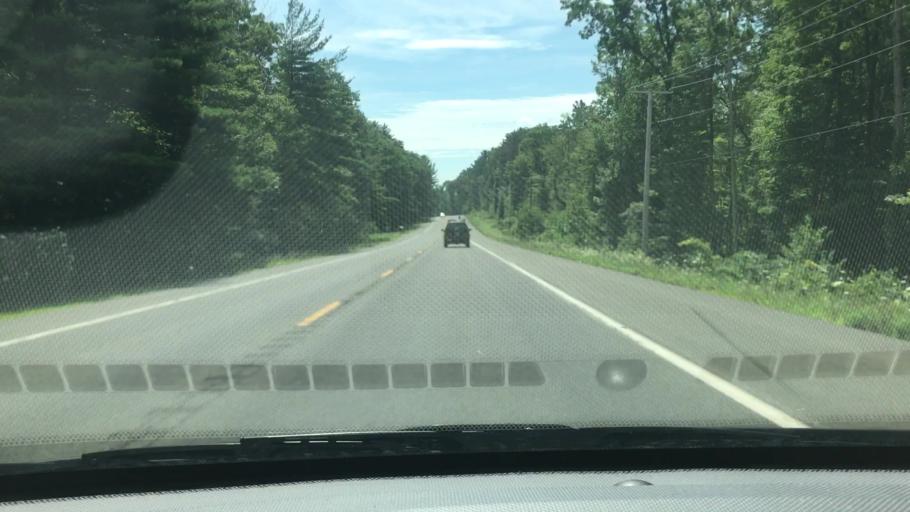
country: US
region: New York
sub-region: Ulster County
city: Shokan
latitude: 41.9814
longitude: -74.2546
